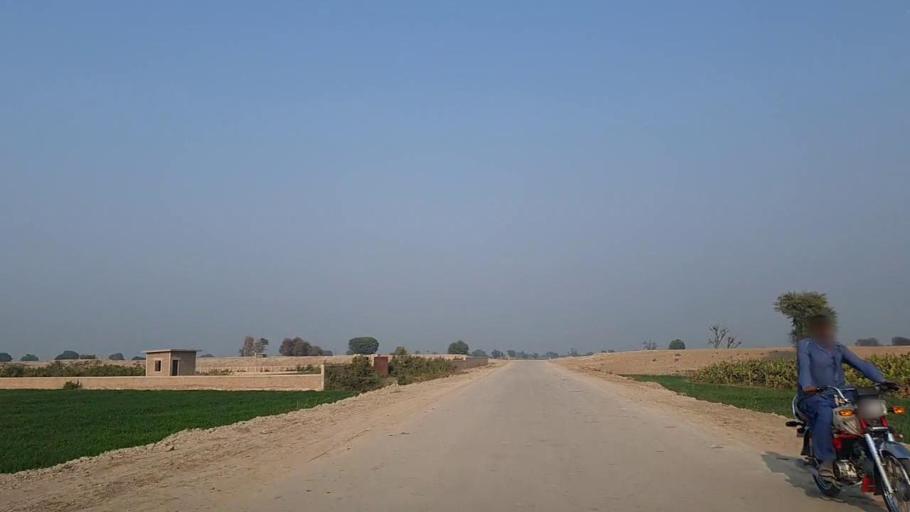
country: PK
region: Sindh
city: Sann
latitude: 26.1273
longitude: 68.1471
